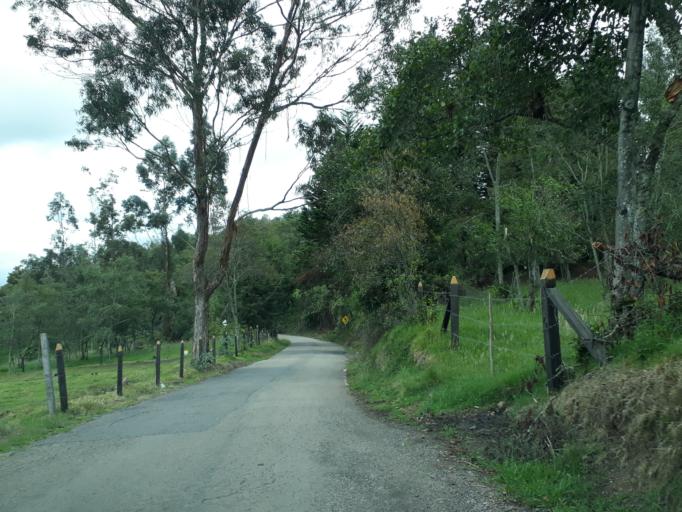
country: CO
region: Cundinamarca
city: Susa
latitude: 5.4001
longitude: -73.7972
